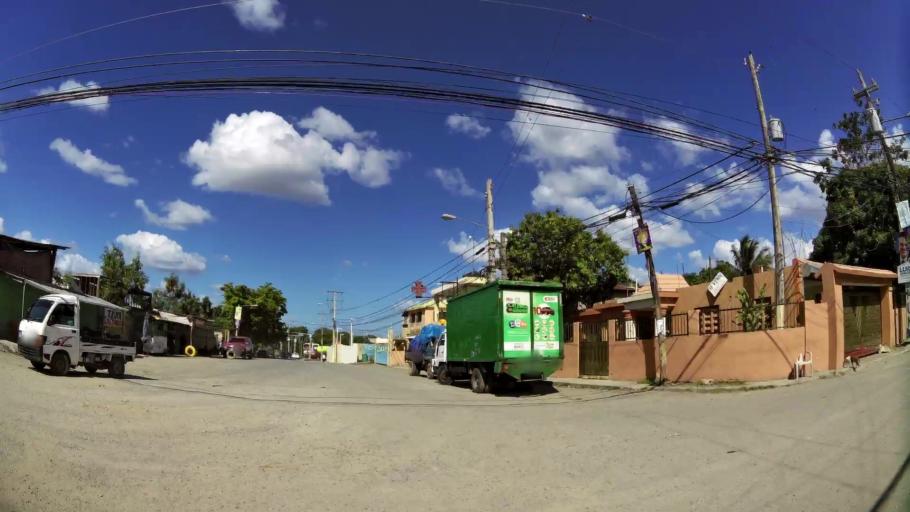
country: DO
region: Santo Domingo
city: Santo Domingo Oeste
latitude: 18.5447
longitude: -70.0399
